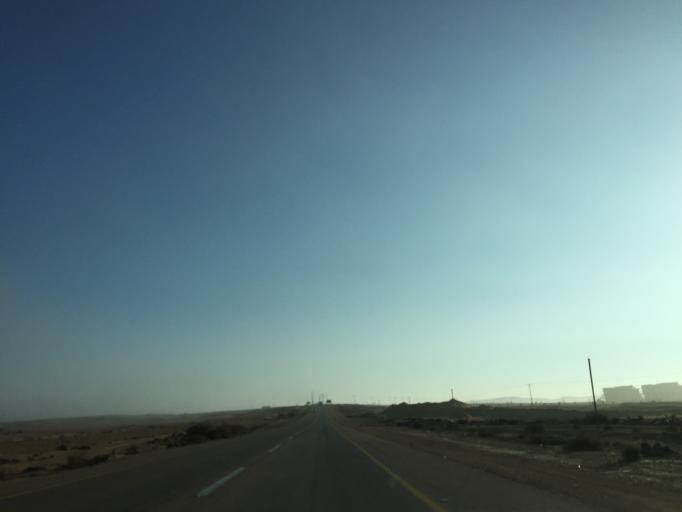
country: IL
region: Southern District
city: Yeroham
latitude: 30.9972
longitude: 34.9335
